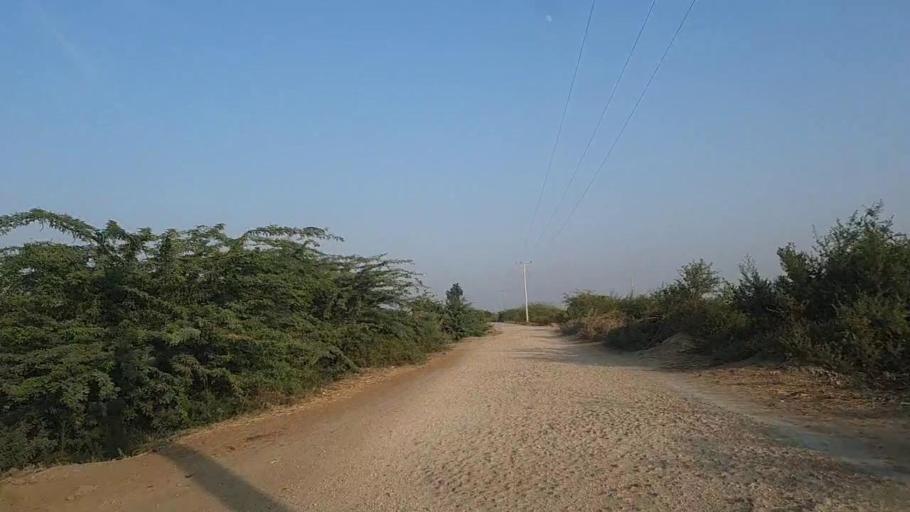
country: PK
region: Sindh
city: Keti Bandar
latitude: 24.2768
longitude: 67.6569
